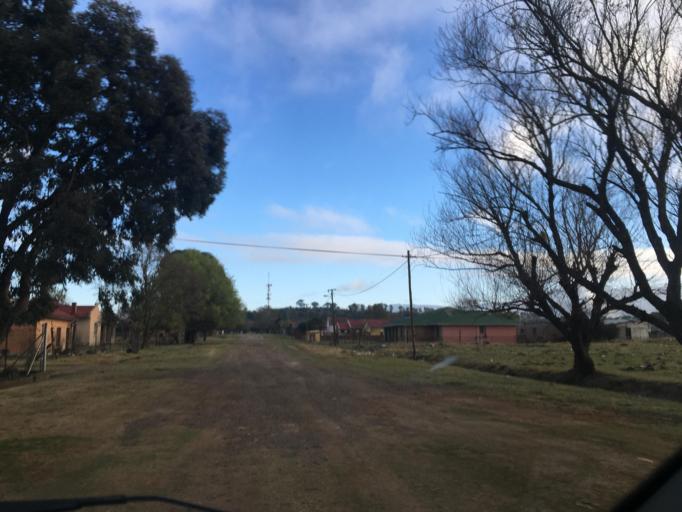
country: ZA
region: Eastern Cape
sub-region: Chris Hani District Municipality
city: Elliot
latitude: -31.3380
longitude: 27.8520
